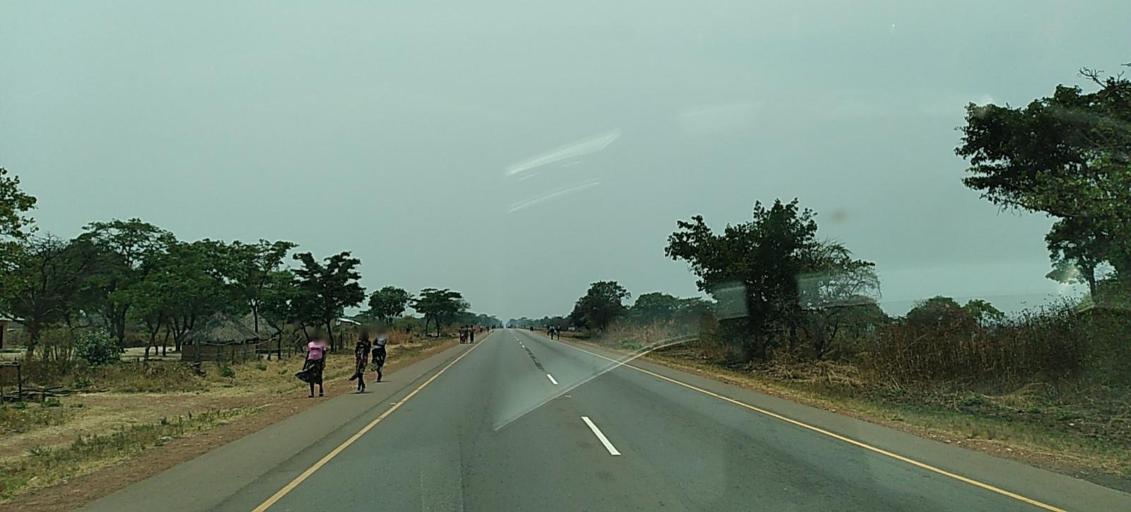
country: CD
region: Katanga
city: Kipushi
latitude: -12.3358
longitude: 27.0690
